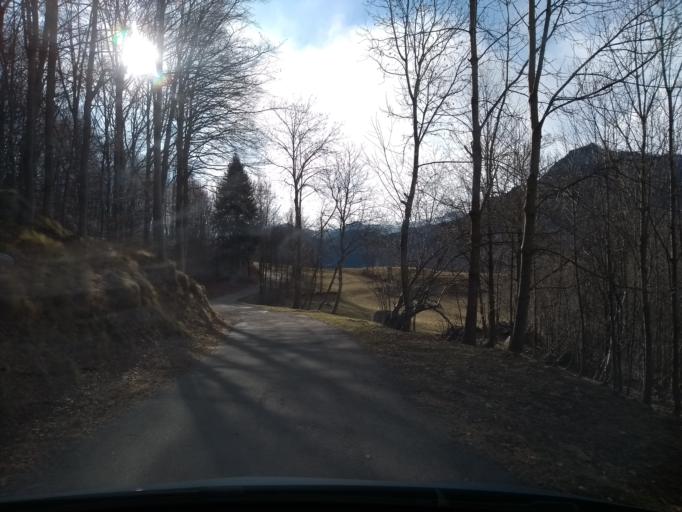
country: IT
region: Piedmont
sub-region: Provincia di Torino
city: Cantoira
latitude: 45.3519
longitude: 7.3842
